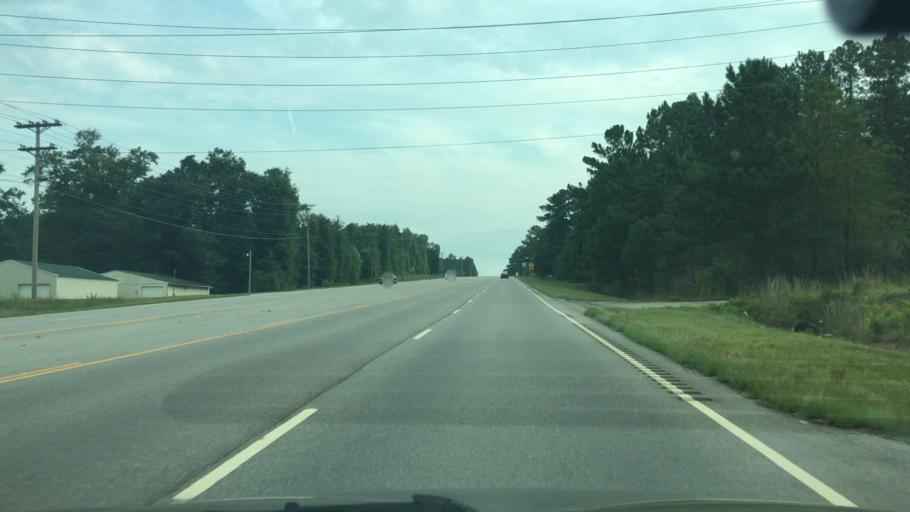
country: US
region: South Carolina
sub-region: Aiken County
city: Aiken
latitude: 33.6376
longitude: -81.6770
